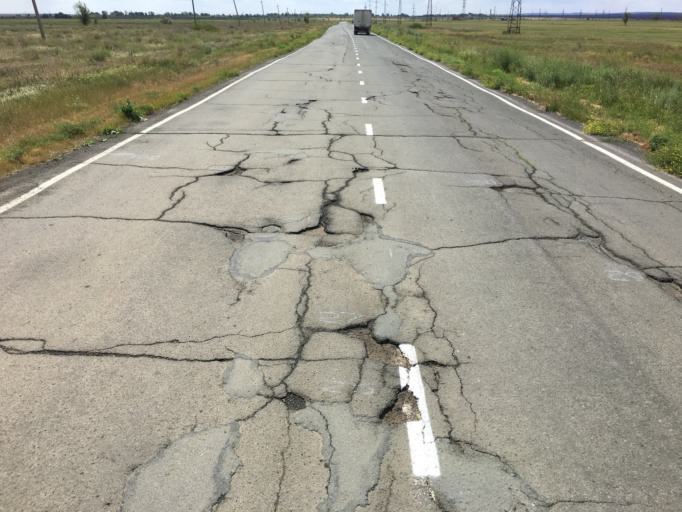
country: RU
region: Orenburg
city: Novotroitsk
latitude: 51.1551
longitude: 58.3409
